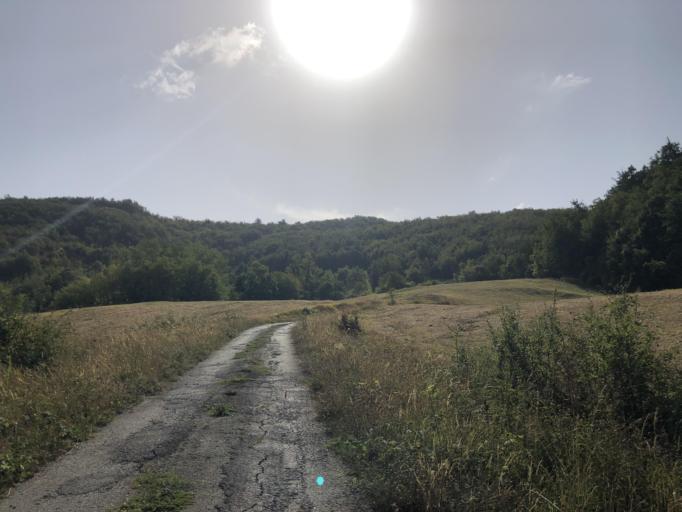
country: IT
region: Emilia-Romagna
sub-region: Forli-Cesena
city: Portico e San Benedetto
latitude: 44.0165
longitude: 11.7869
